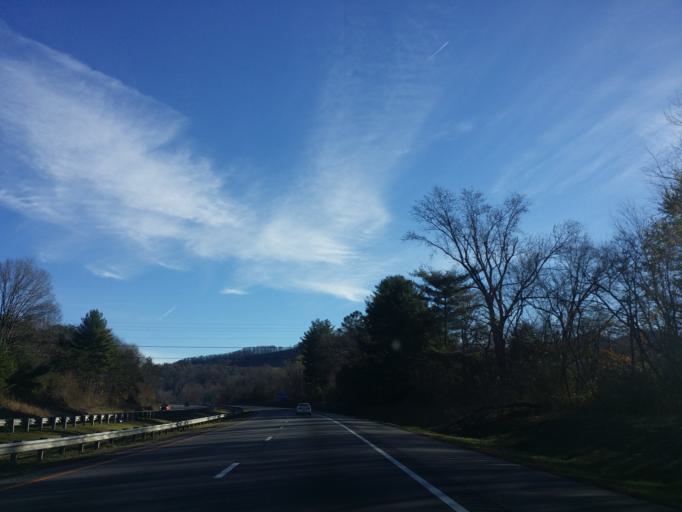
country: US
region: North Carolina
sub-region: Buncombe County
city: Black Mountain
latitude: 35.6073
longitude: -82.3284
